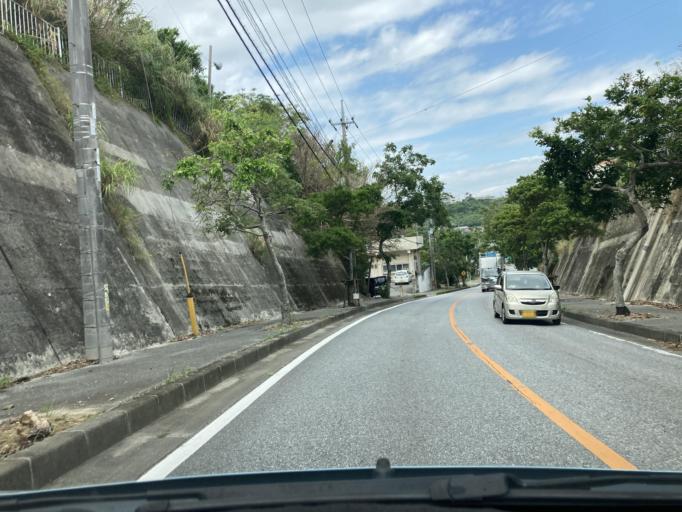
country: JP
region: Okinawa
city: Ginowan
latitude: 26.2710
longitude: 127.7811
